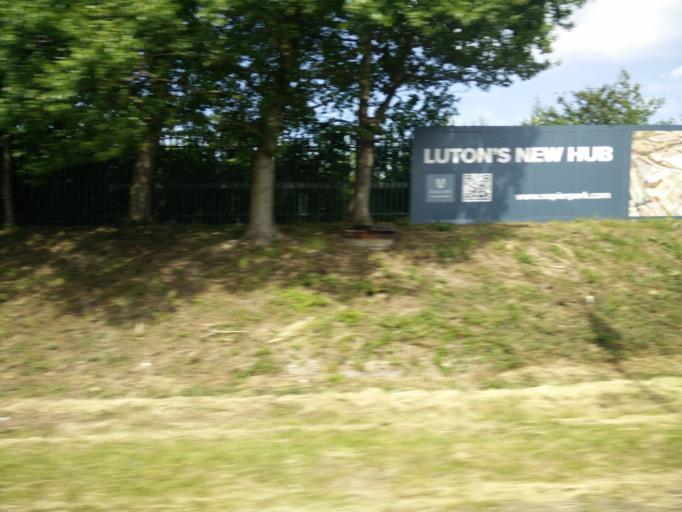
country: GB
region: England
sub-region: Luton
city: Luton
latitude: 51.8740
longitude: -0.3953
